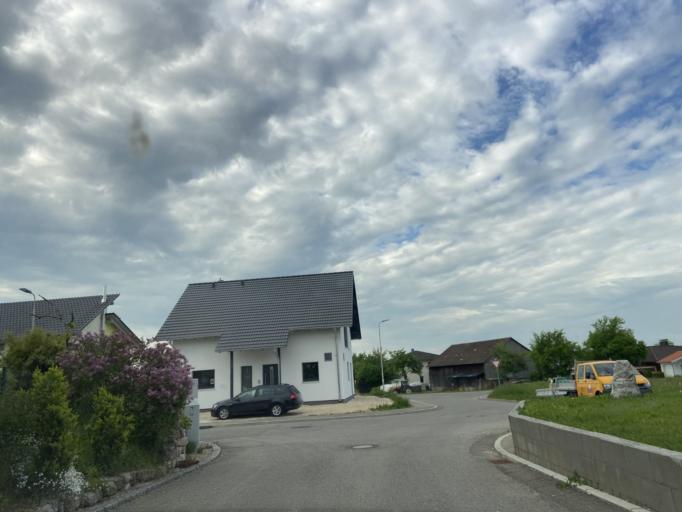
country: DE
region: Baden-Wuerttemberg
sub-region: Tuebingen Region
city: Scheer
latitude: 48.0708
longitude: 9.3044
